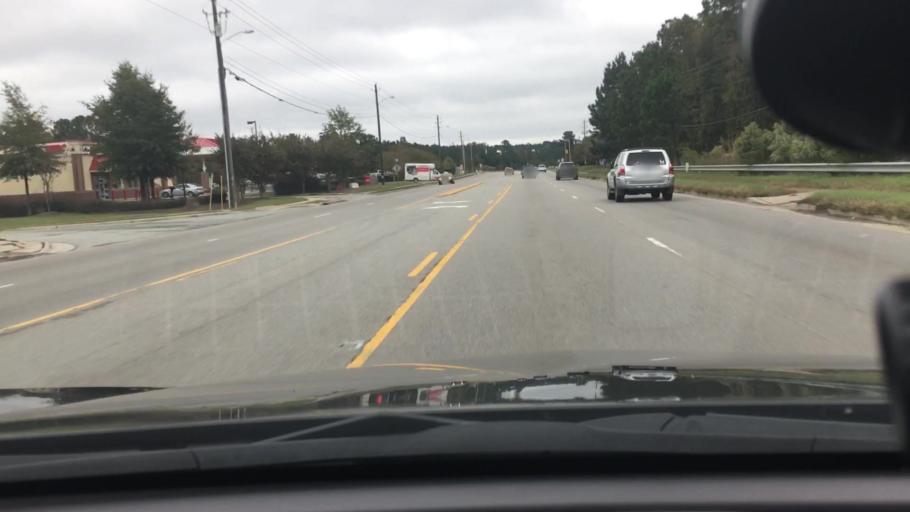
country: US
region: North Carolina
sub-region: Wake County
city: Apex
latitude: 35.7074
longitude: -78.8365
